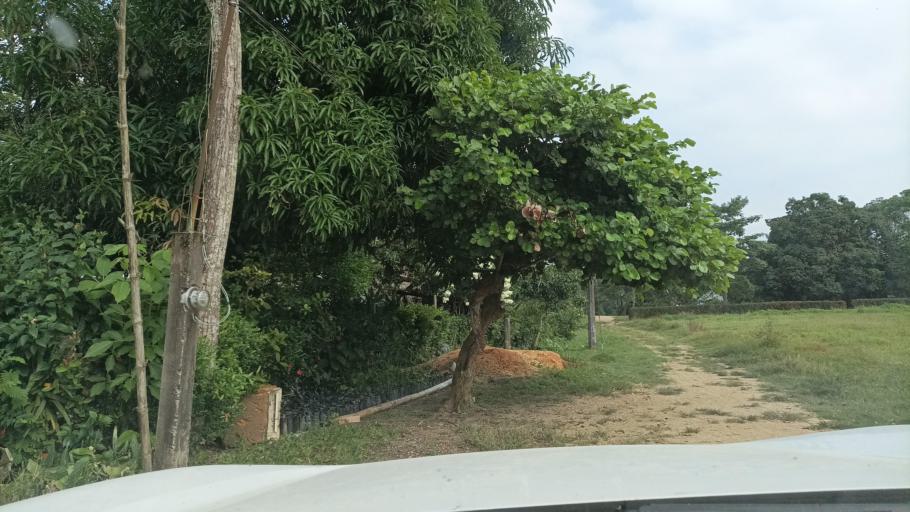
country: MX
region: Veracruz
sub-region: Texistepec
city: San Lorenzo Tenochtitlan
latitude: 17.8156
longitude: -94.7869
